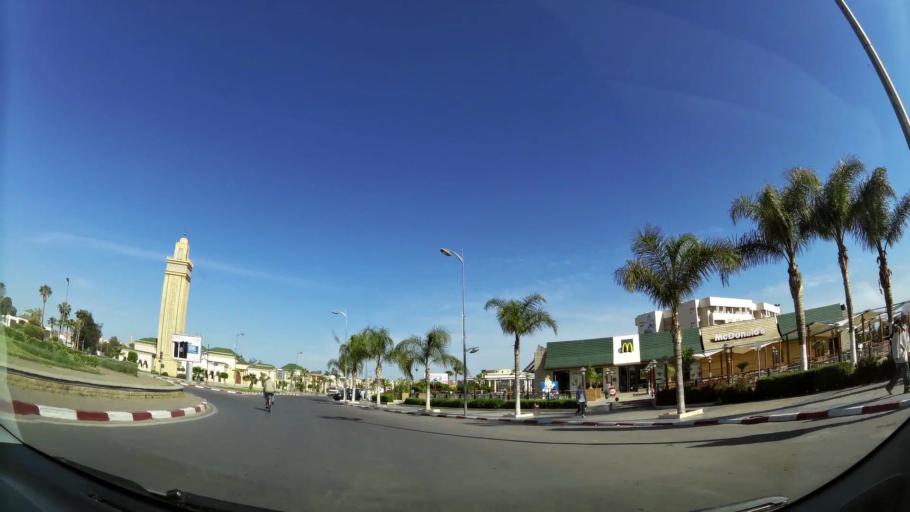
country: MA
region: Oriental
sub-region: Oujda-Angad
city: Oujda
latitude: 34.6765
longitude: -1.9277
